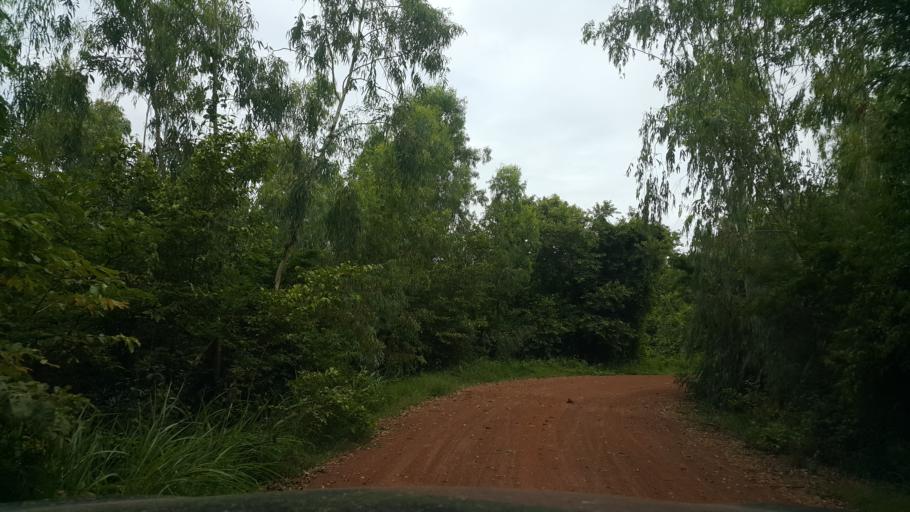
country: TH
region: Phitsanulok
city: Bang Rakam
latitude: 16.8420
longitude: 100.0643
